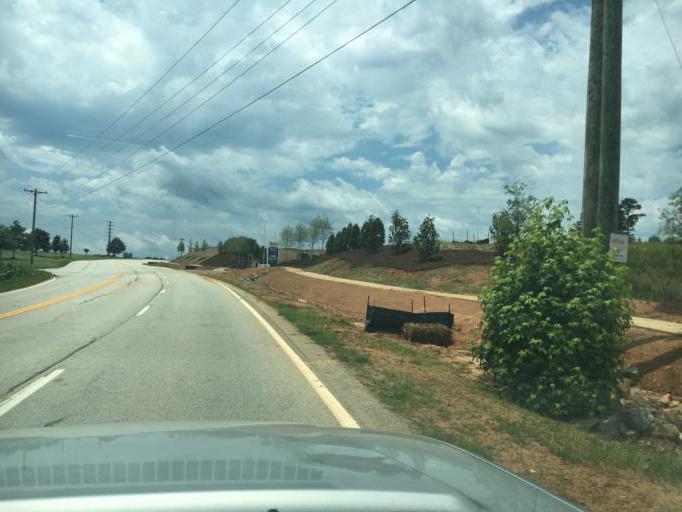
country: US
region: South Carolina
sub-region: Spartanburg County
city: Duncan
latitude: 34.8714
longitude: -82.1621
